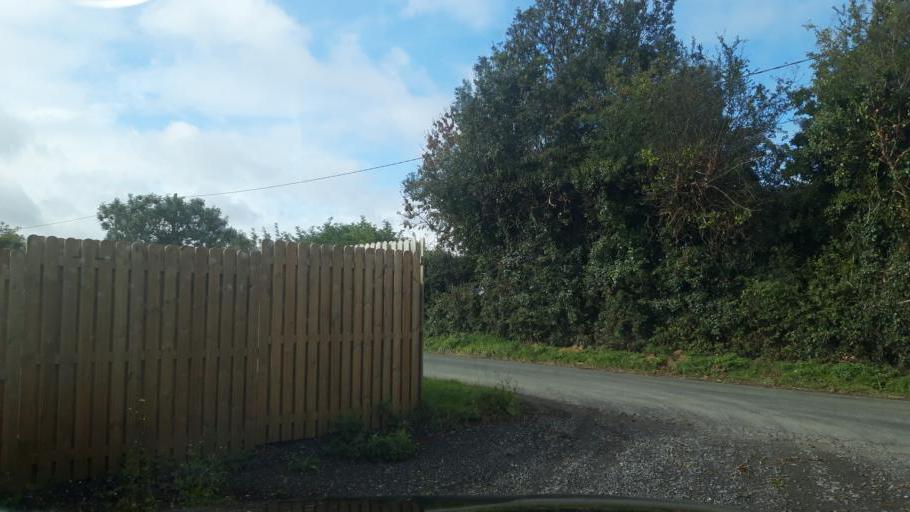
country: IE
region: Leinster
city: Ballymun
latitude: 53.4612
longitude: -6.2950
